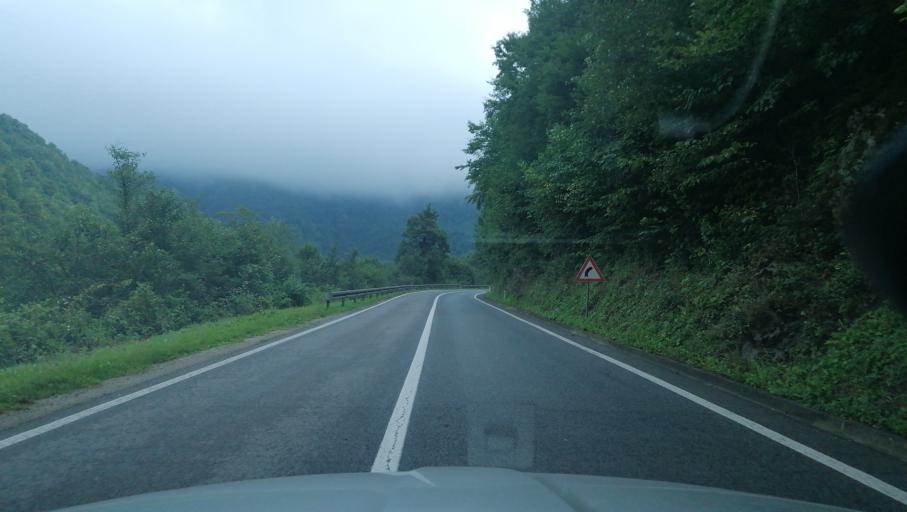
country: BA
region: Federation of Bosnia and Herzegovina
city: Donji Vakuf
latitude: 44.1983
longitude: 17.3348
